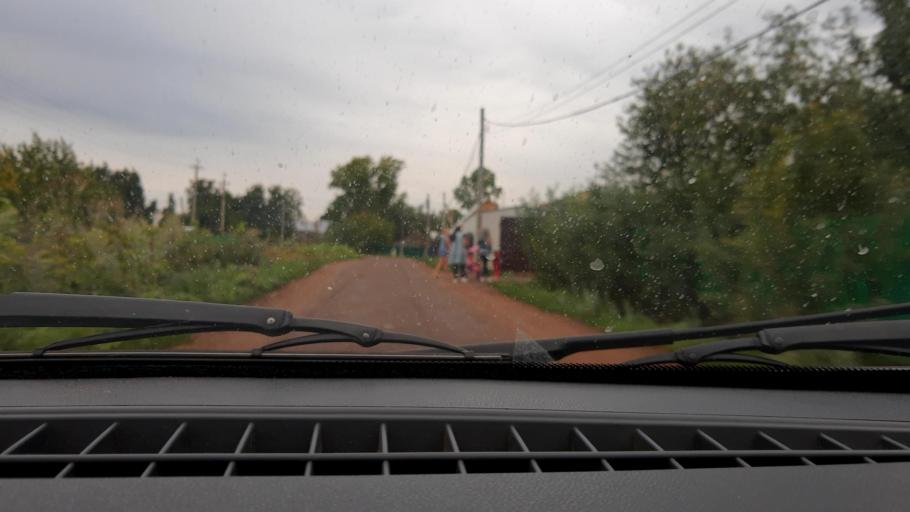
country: RU
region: Bashkortostan
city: Mikhaylovka
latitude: 54.8614
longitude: 55.8102
